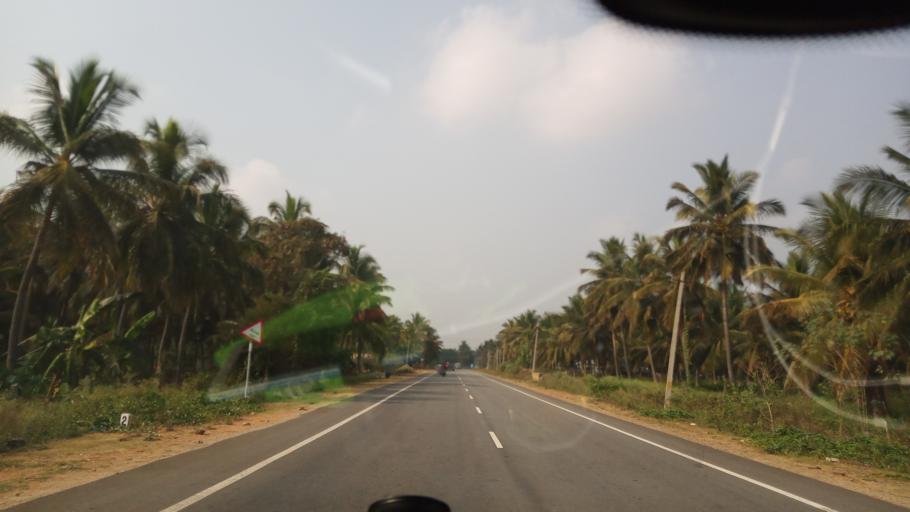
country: IN
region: Karnataka
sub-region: Mandya
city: Nagamangala
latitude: 12.7719
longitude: 76.7402
